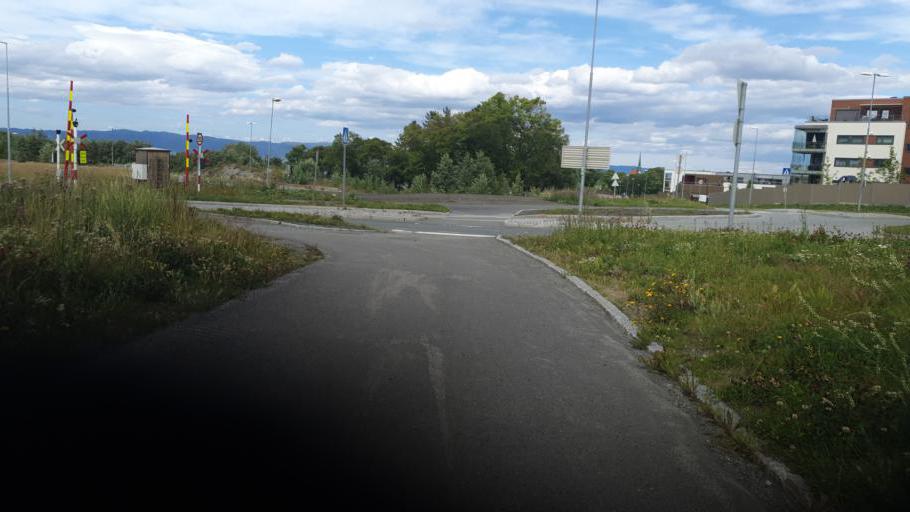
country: NO
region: Sor-Trondelag
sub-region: Klaebu
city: Klaebu
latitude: 63.4247
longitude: 10.5354
